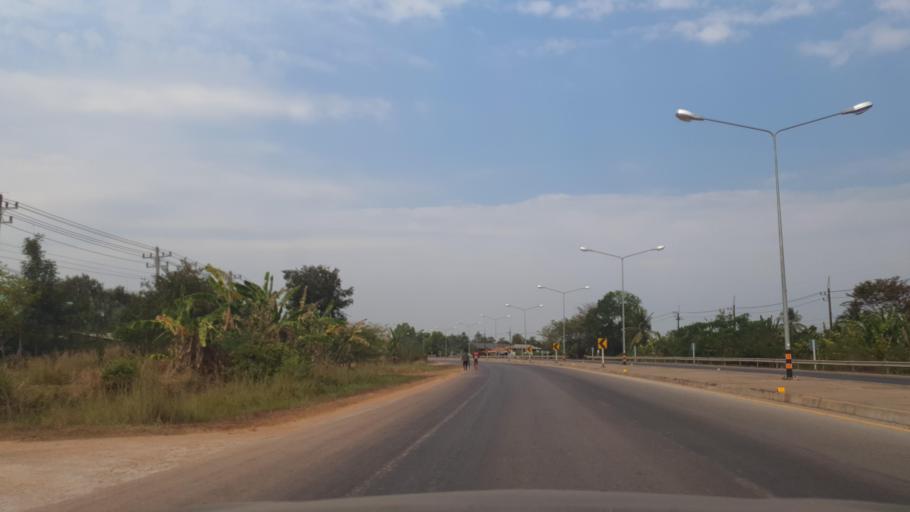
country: TH
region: Changwat Bueng Kan
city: Si Wilai
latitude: 18.3024
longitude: 103.8150
